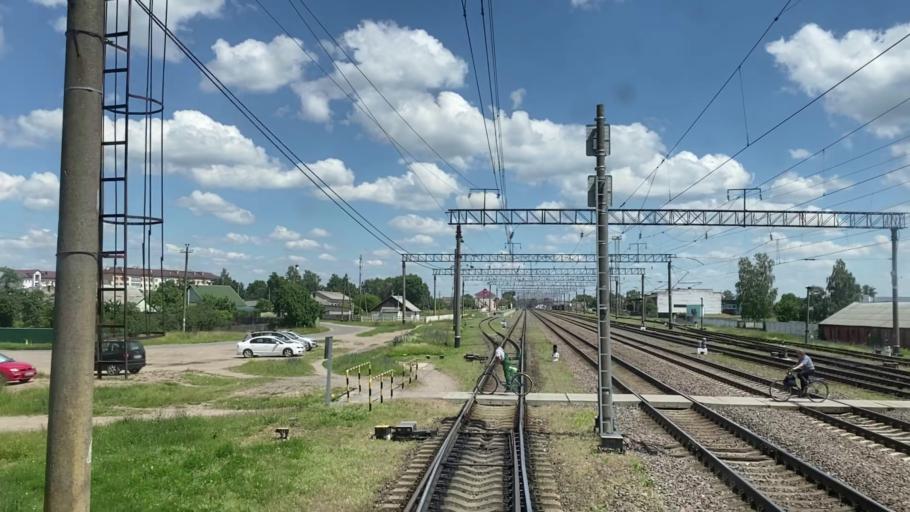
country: BY
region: Brest
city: Ivatsevichy
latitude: 52.7050
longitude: 25.3354
